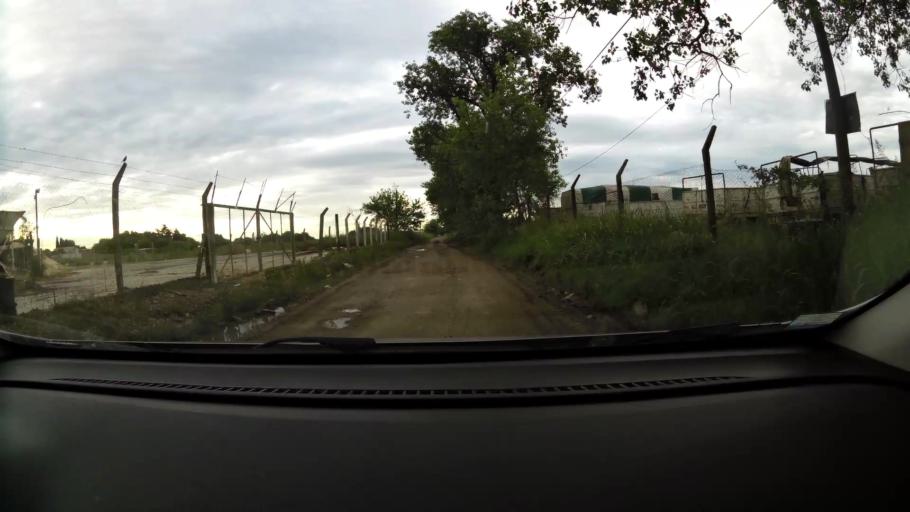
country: AR
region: Buenos Aires
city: San Nicolas de los Arroyos
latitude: -33.3694
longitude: -60.2010
